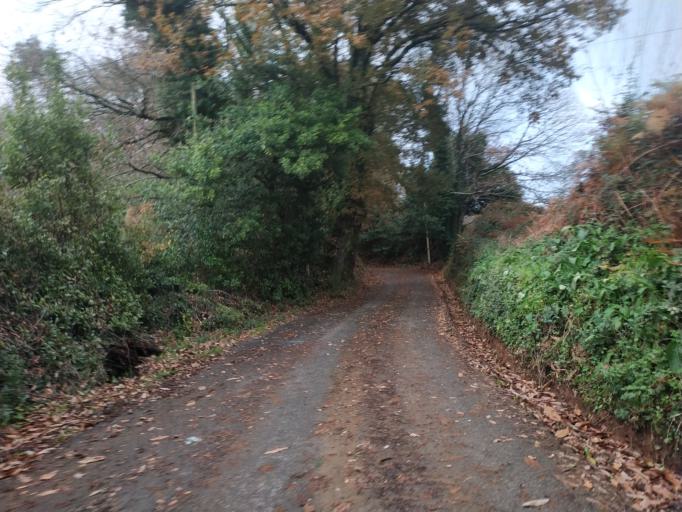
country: ES
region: Galicia
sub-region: Provincia de Pontevedra
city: Silleda
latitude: 42.7822
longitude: -8.1646
